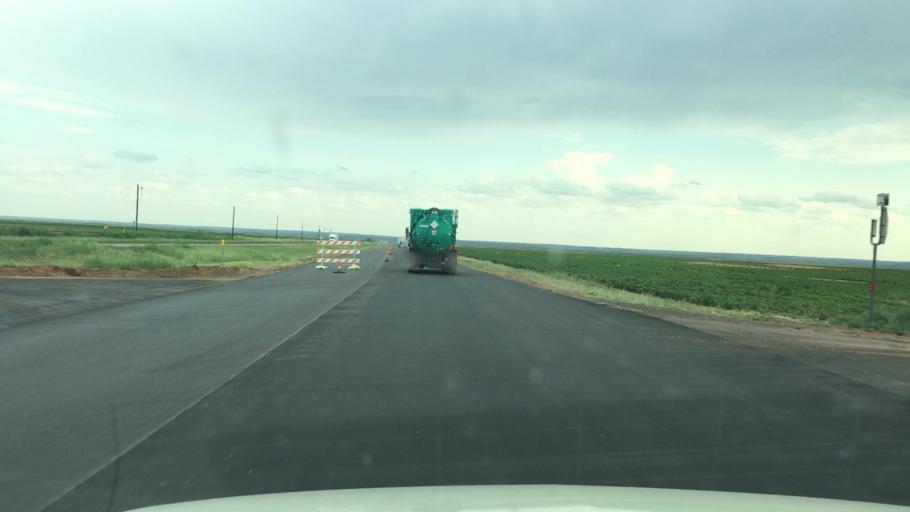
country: US
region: Texas
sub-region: Hall County
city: Memphis
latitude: 34.6307
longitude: -100.4760
